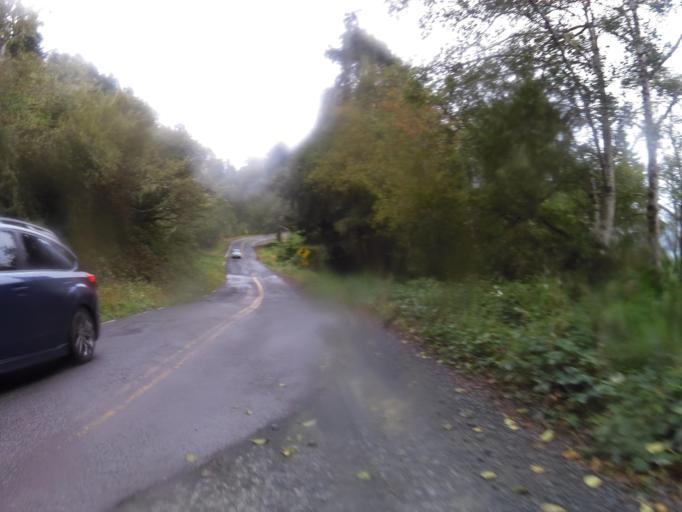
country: US
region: California
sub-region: Humboldt County
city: Westhaven-Moonstone
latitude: 41.1056
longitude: -124.1595
